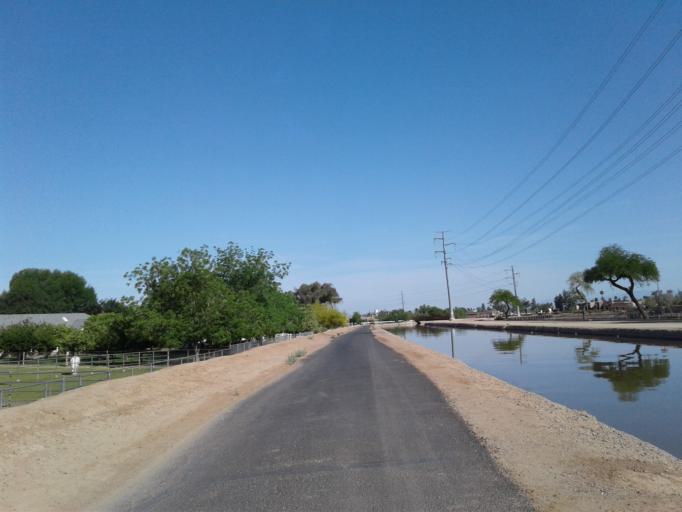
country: US
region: Arizona
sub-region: Maricopa County
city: Glendale
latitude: 33.5910
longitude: -112.1650
